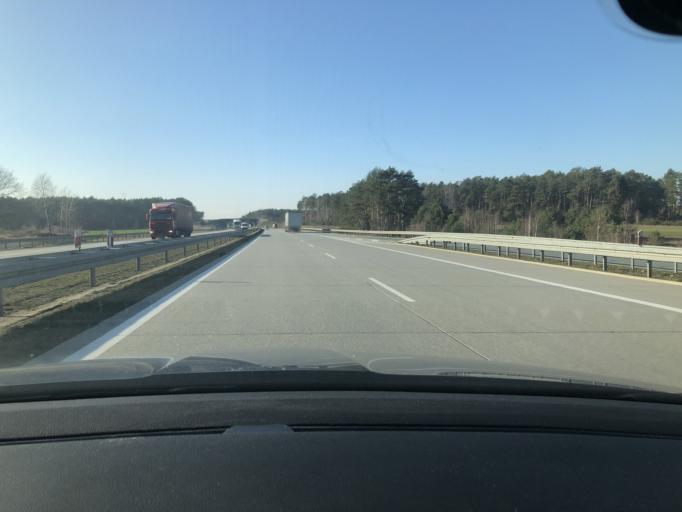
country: PL
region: Lubusz
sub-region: Powiat sulecinski
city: Torzym
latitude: 52.3261
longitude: 15.1604
